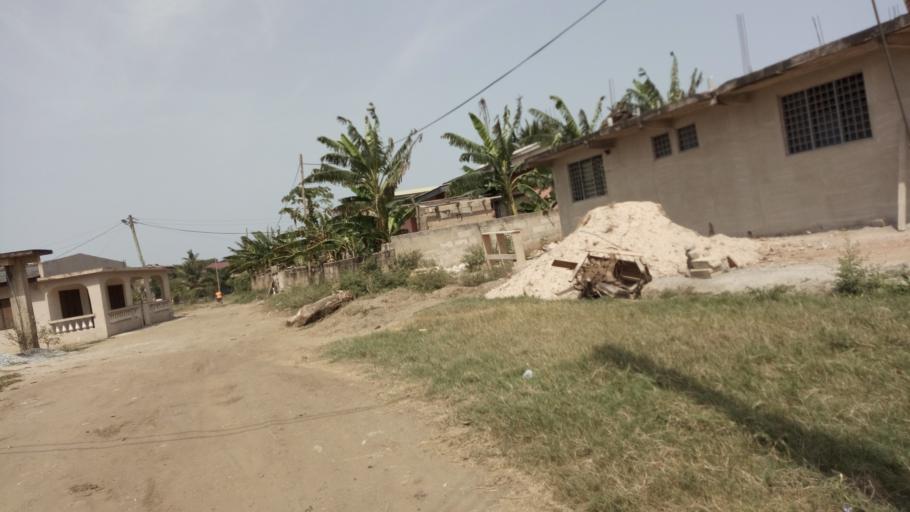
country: GH
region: Central
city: Winneba
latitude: 5.3586
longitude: -0.6372
